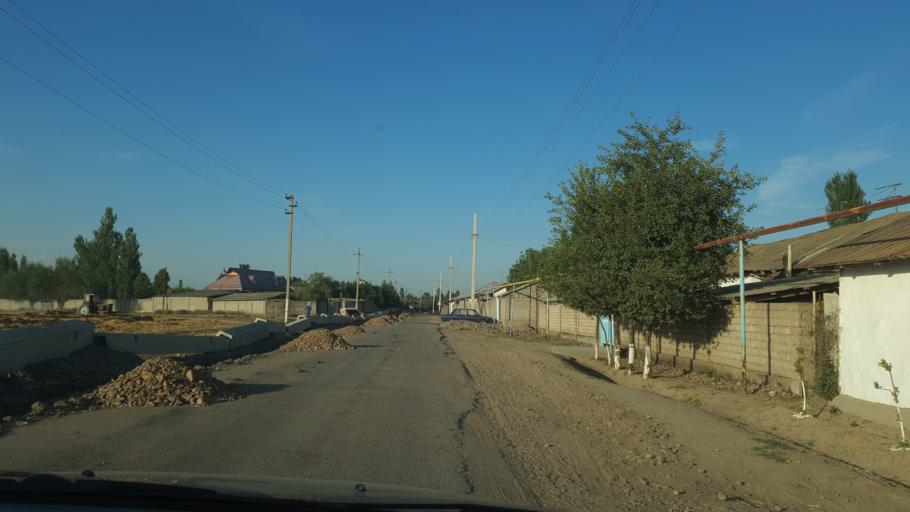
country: UZ
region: Toshkent
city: Tuytepa
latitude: 41.1035
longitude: 69.3877
